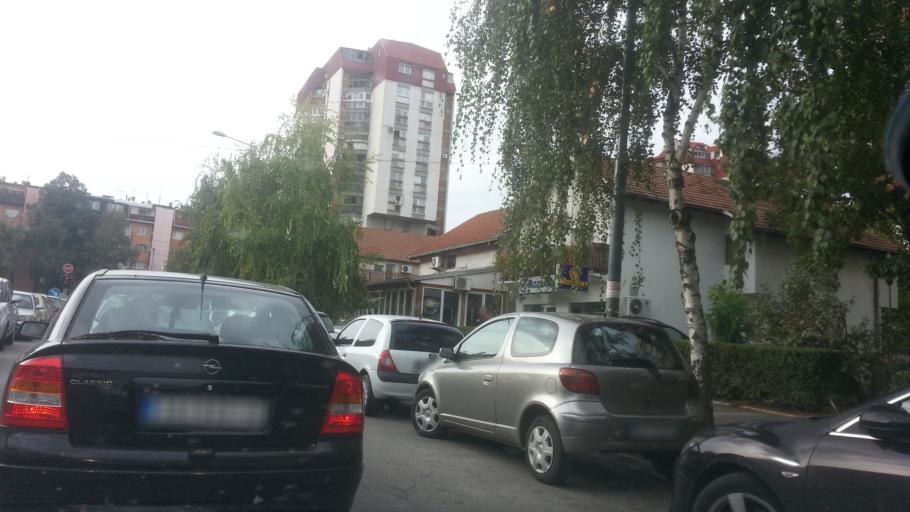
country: RS
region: Central Serbia
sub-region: Belgrade
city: Zemun
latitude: 44.8417
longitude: 20.3932
